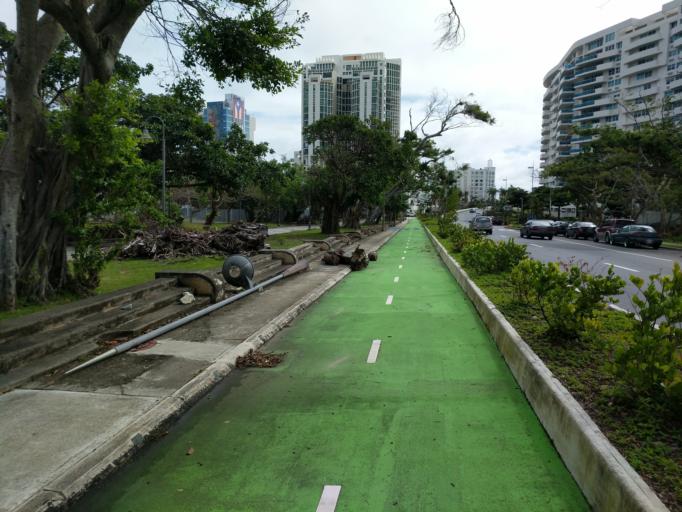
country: PR
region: San Juan
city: San Juan
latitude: 18.4631
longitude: -66.0898
